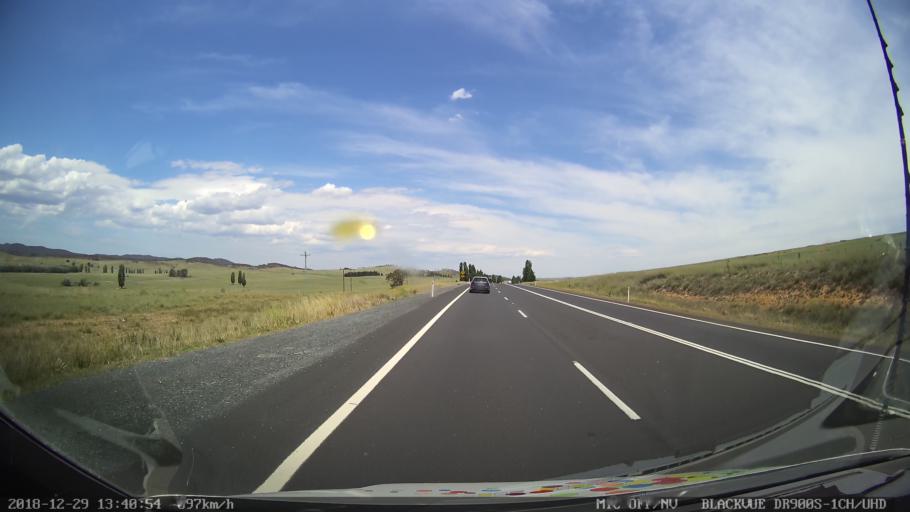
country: AU
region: New South Wales
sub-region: Cooma-Monaro
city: Cooma
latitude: -36.0339
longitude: 149.1546
